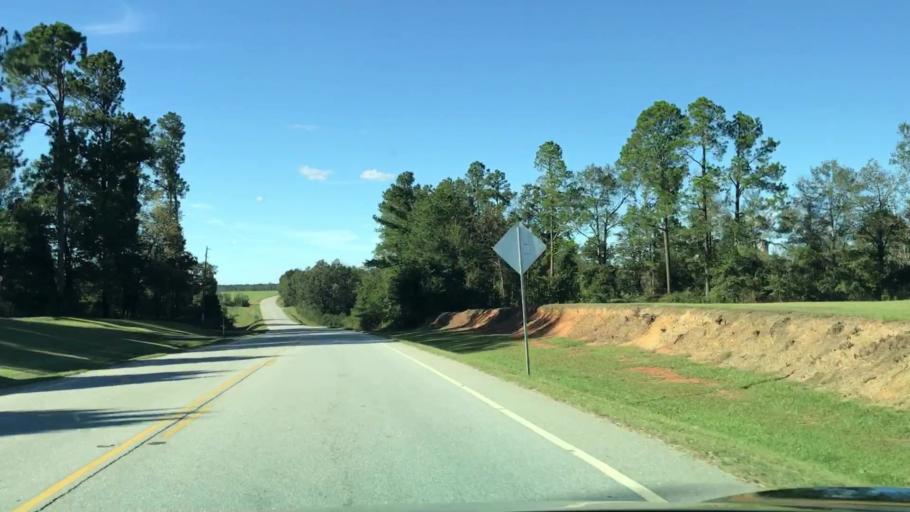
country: US
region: Georgia
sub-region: Jefferson County
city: Louisville
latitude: 33.0704
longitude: -82.4075
